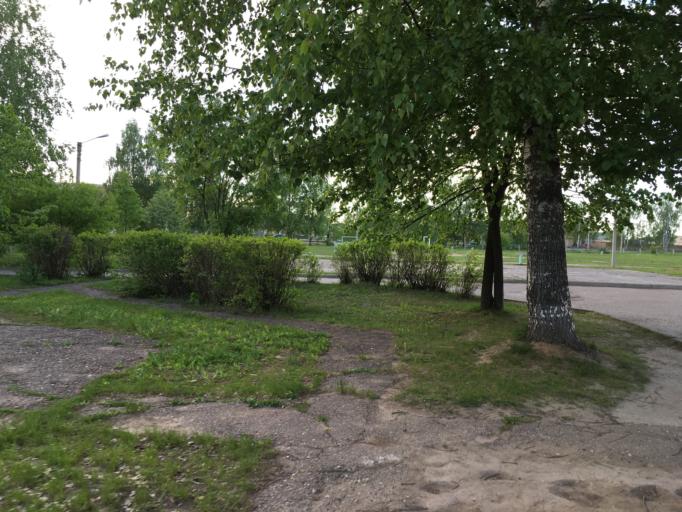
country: RU
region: Mariy-El
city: Yoshkar-Ola
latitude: 56.6525
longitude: 47.8688
